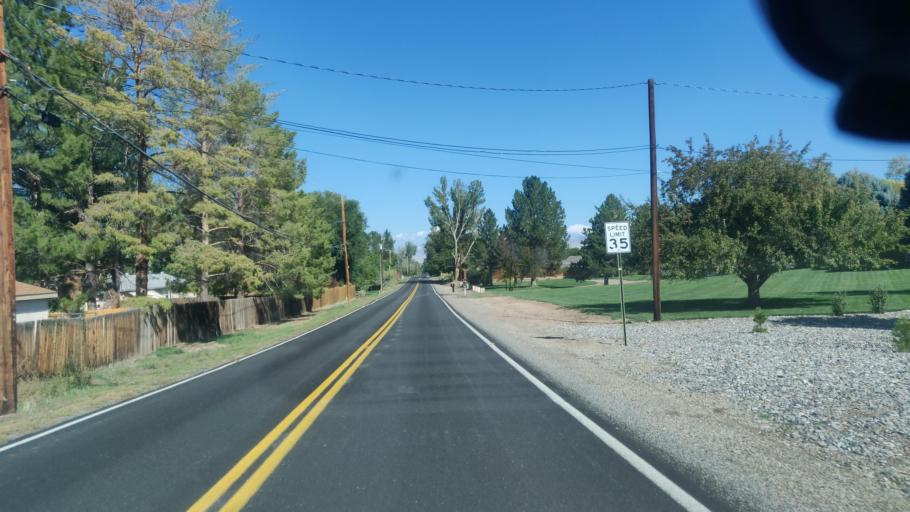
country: US
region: Colorado
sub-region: Mesa County
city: Redlands
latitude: 39.0775
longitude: -108.6265
